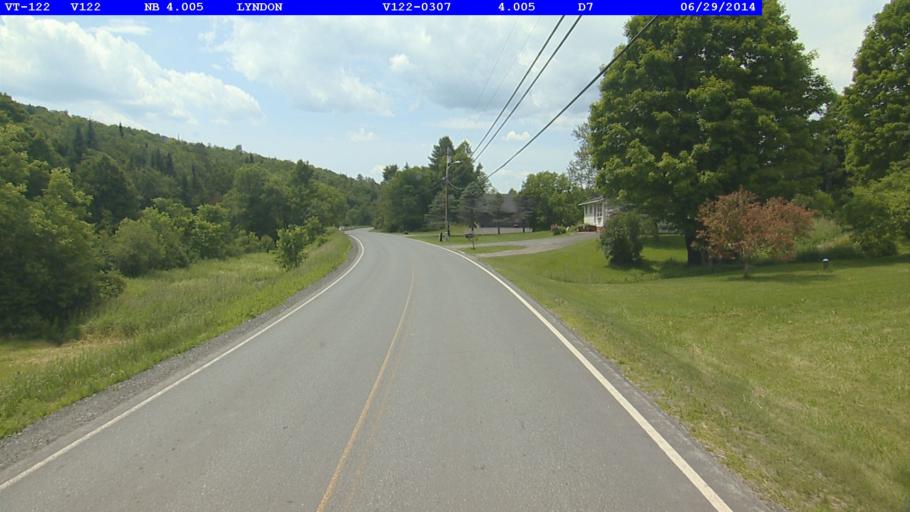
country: US
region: Vermont
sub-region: Caledonia County
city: Lyndonville
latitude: 44.5773
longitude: -72.0569
